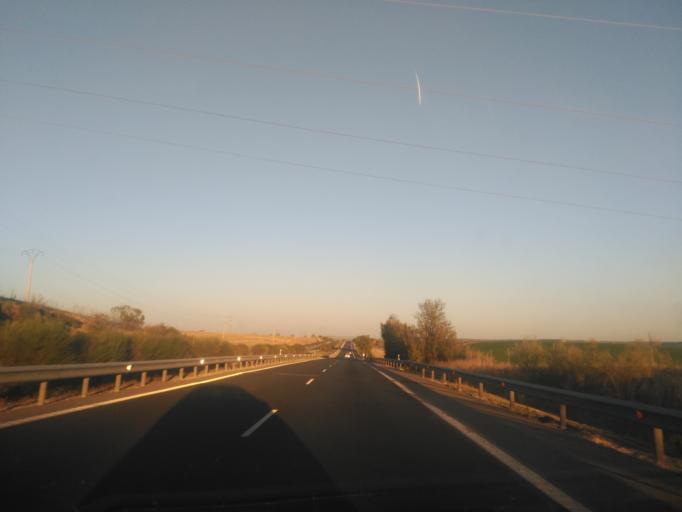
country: ES
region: Castille and Leon
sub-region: Provincia de Valladolid
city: Cisterniga
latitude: 41.5971
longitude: -4.6458
